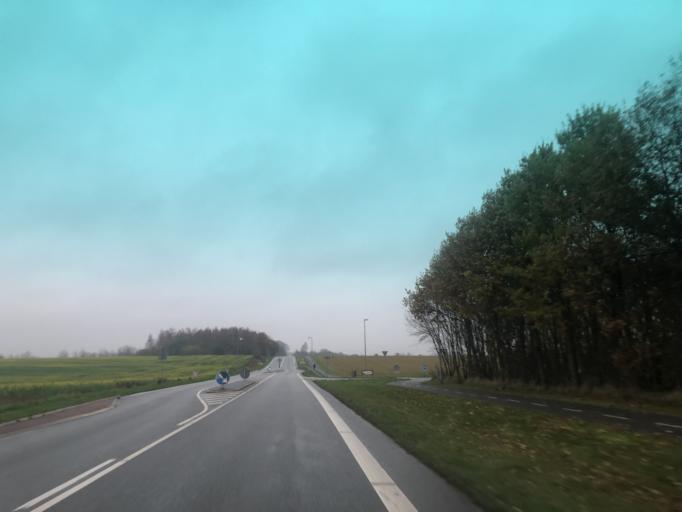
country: DK
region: South Denmark
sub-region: Nyborg Kommune
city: Ullerslev
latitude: 55.2790
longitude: 10.6862
